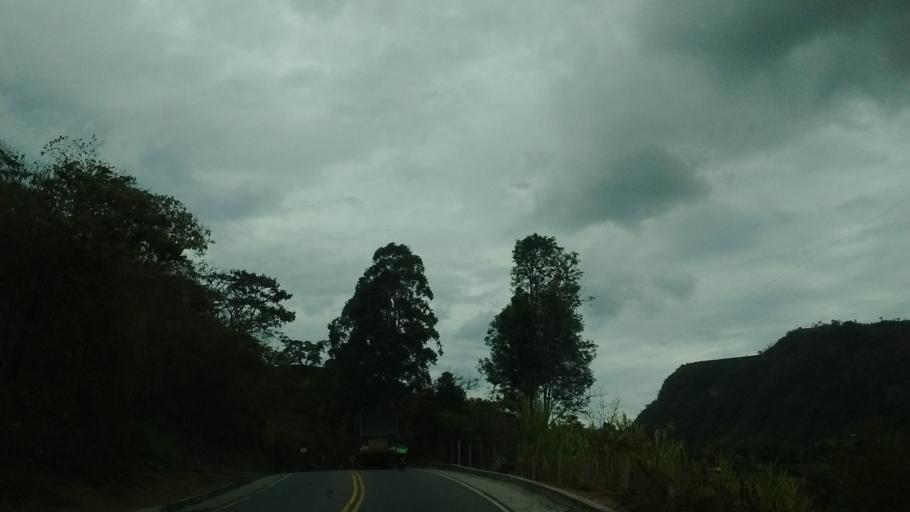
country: CO
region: Cauca
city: Rosas
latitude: 2.2664
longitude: -76.7353
